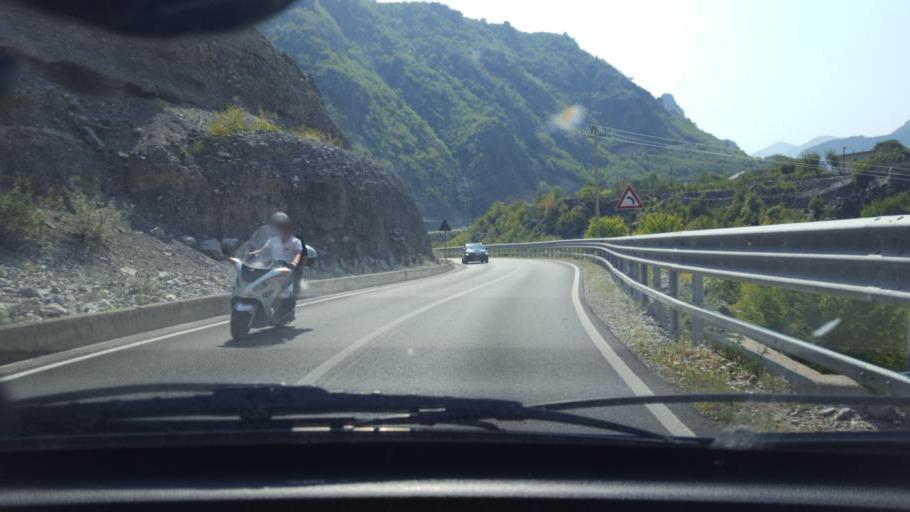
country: AL
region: Shkoder
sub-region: Rrethi i Malesia e Madhe
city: Kastrat
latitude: 42.4570
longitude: 19.5612
